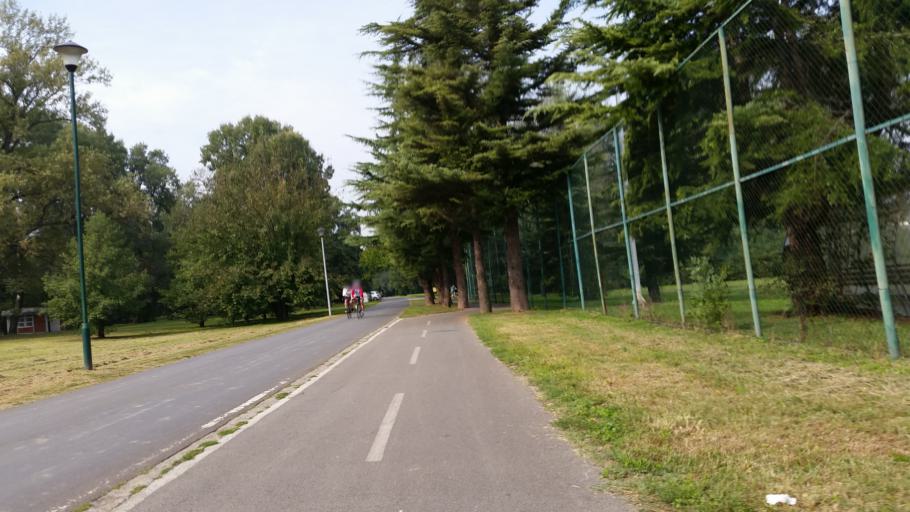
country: RS
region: Central Serbia
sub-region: Belgrade
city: Cukarica
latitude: 44.7883
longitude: 20.3969
